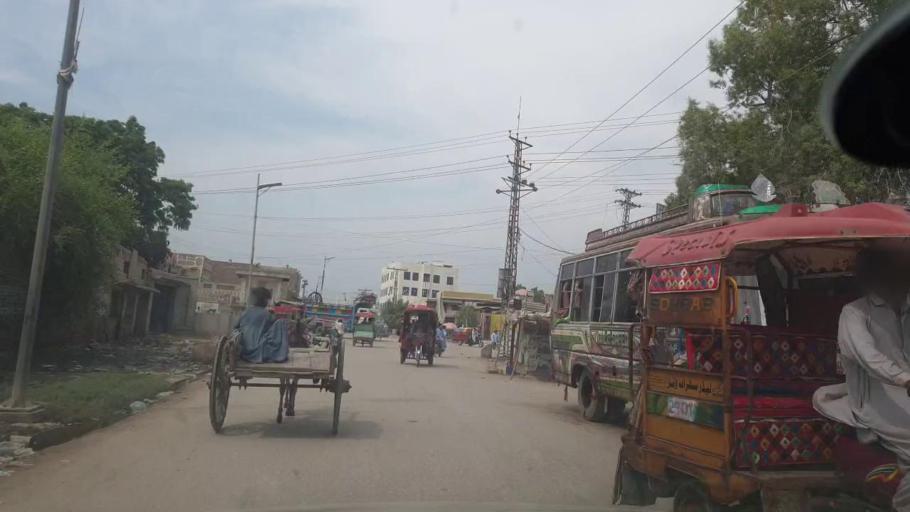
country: PK
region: Sindh
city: Jacobabad
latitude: 28.2782
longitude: 68.4382
